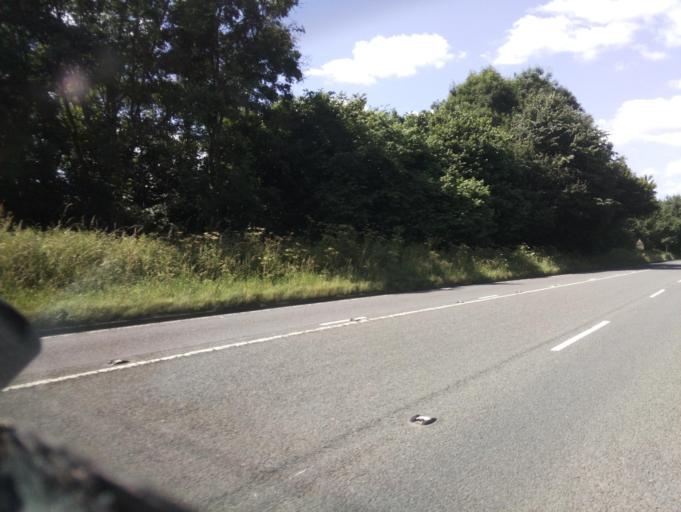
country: GB
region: England
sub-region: Derbyshire
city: Ashbourne
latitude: 53.0064
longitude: -1.7355
